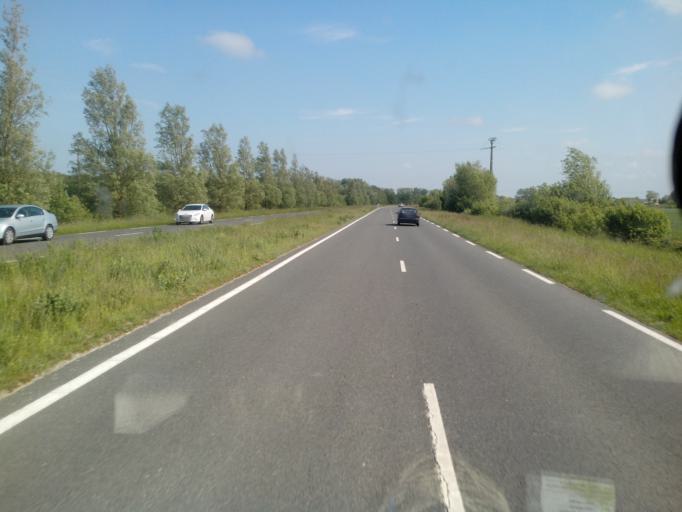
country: FR
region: Picardie
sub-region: Departement de la Somme
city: Quend
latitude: 50.3015
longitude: 1.6453
